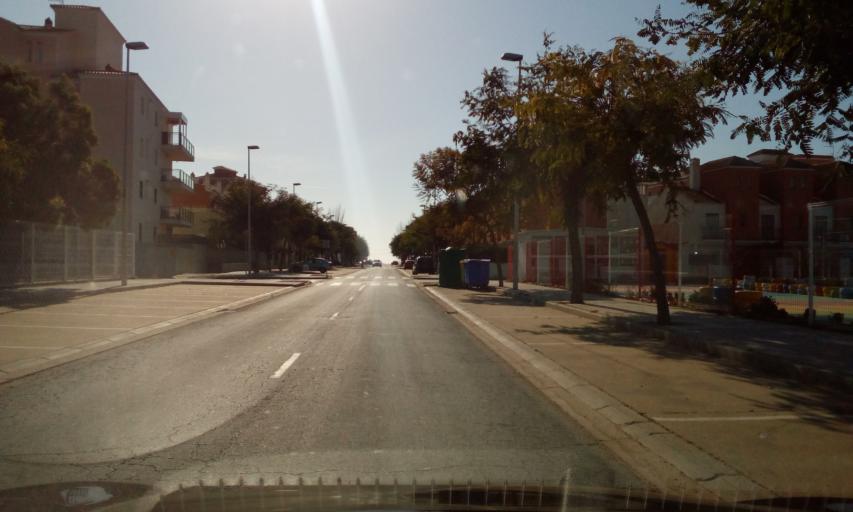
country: ES
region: Andalusia
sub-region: Provincia de Huelva
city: Lepe
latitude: 37.2100
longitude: -7.2034
